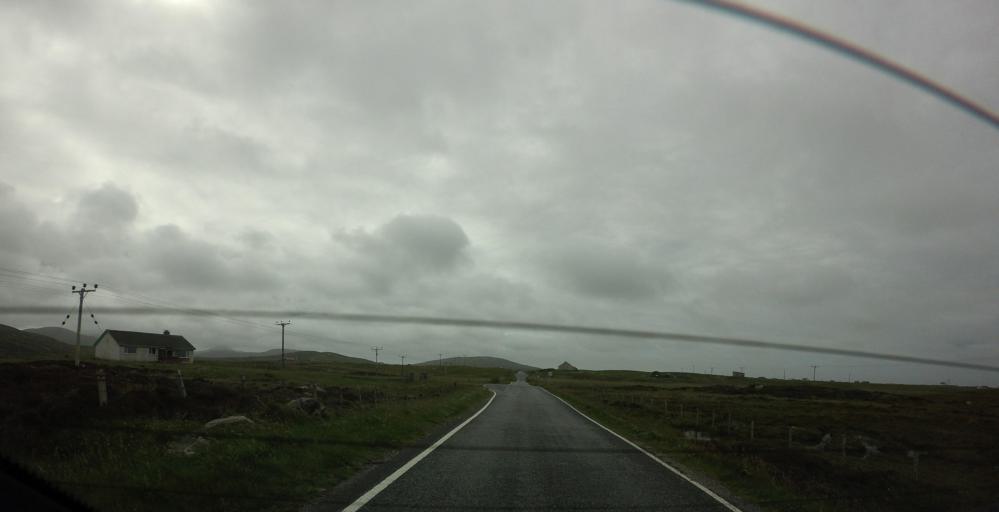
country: GB
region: Scotland
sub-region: Eilean Siar
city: Isle of South Uist
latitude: 57.2182
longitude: -7.3967
